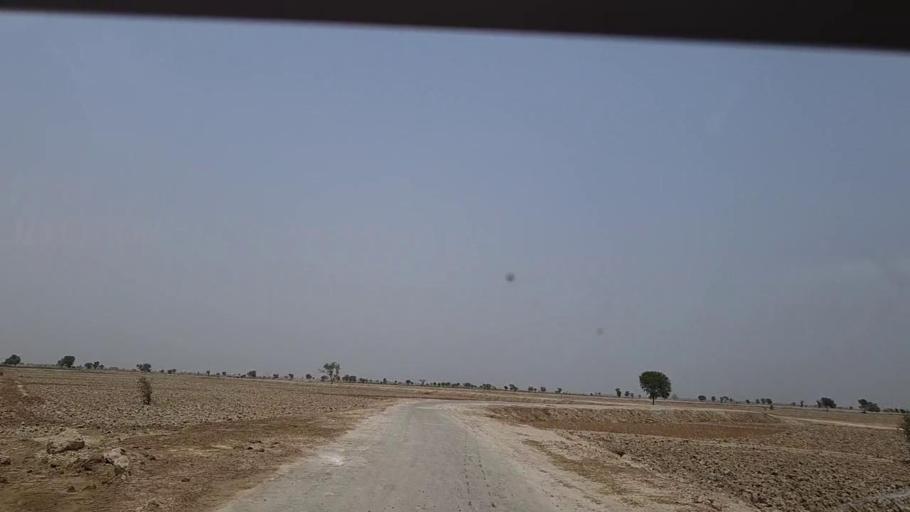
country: PK
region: Sindh
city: Khairpur Nathan Shah
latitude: 27.0145
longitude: 67.6263
